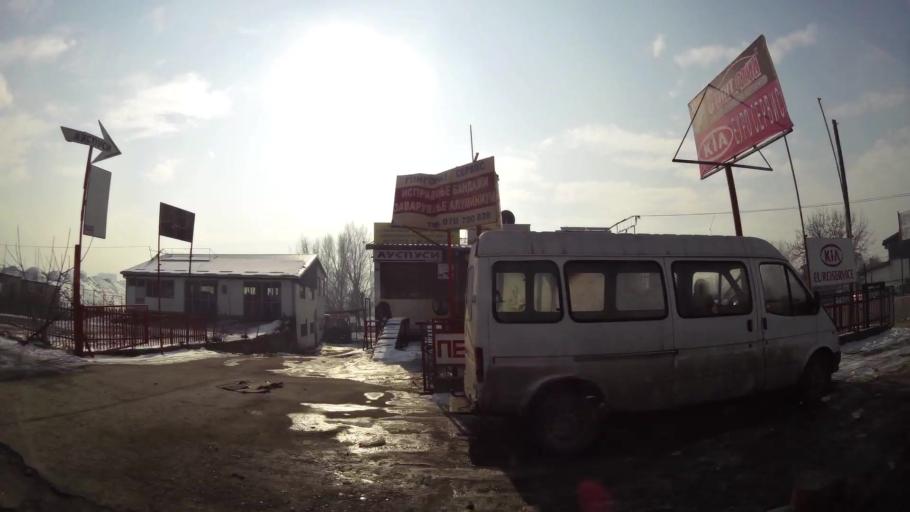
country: MK
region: Suto Orizari
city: Suto Orizare
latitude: 42.0144
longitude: 21.3863
